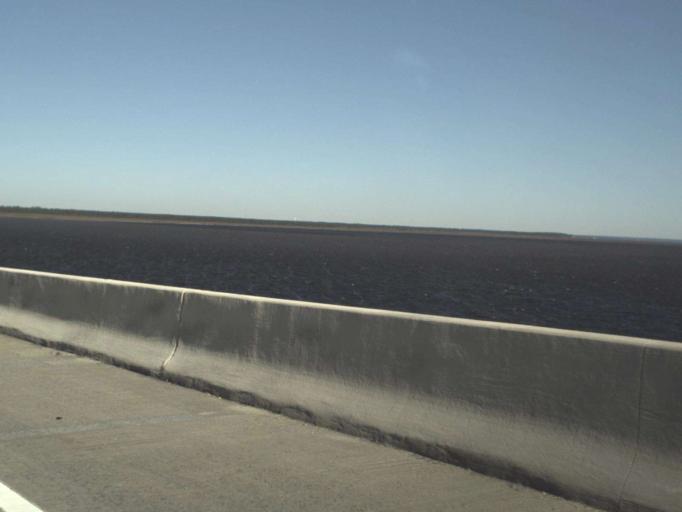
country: US
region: Florida
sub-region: Santa Rosa County
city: Oriole Beach
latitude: 30.4199
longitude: -87.0900
